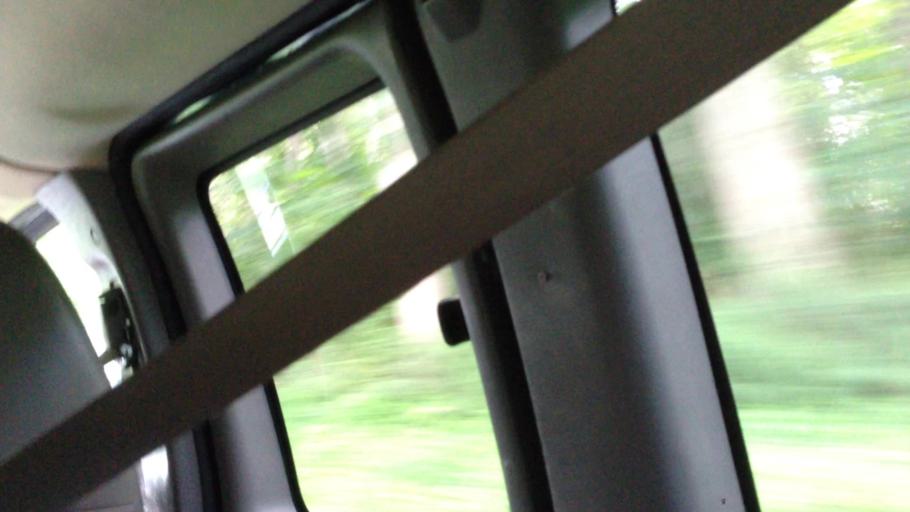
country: US
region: New York
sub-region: Dutchess County
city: Red Hook
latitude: 42.0211
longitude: -73.8922
